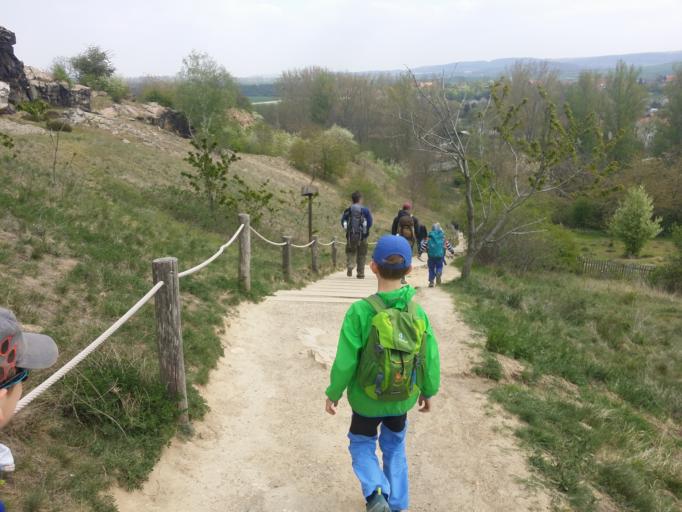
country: DE
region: Saxony-Anhalt
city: Neinstedt
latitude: 51.7568
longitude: 11.0851
